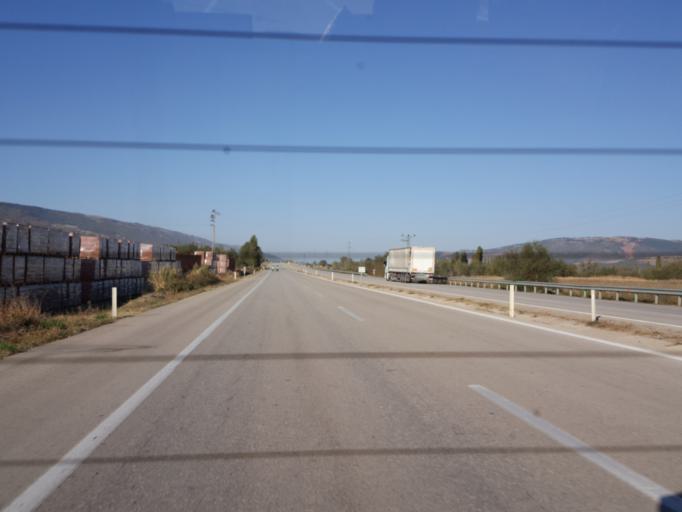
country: TR
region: Amasya
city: Ezinepazari
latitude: 40.5699
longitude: 36.0890
